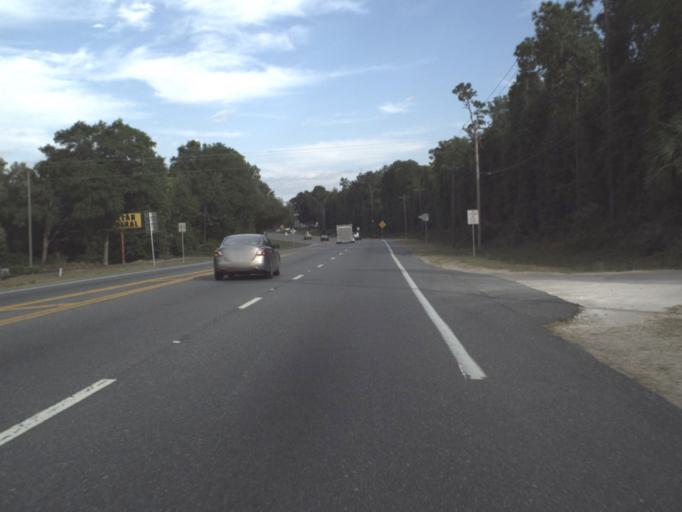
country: US
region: Florida
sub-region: Marion County
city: Silver Springs Shores
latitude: 29.1812
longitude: -81.8876
